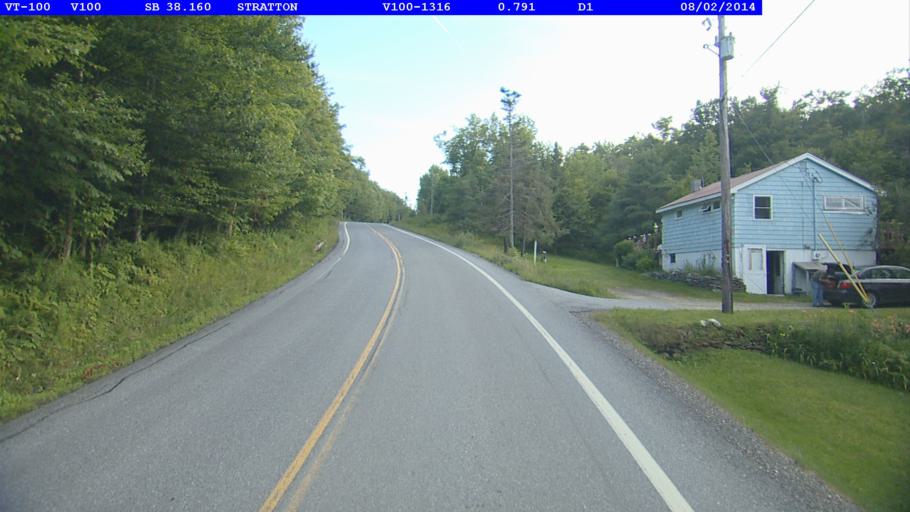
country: US
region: Vermont
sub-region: Windham County
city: Dover
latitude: 43.0024
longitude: -72.8854
